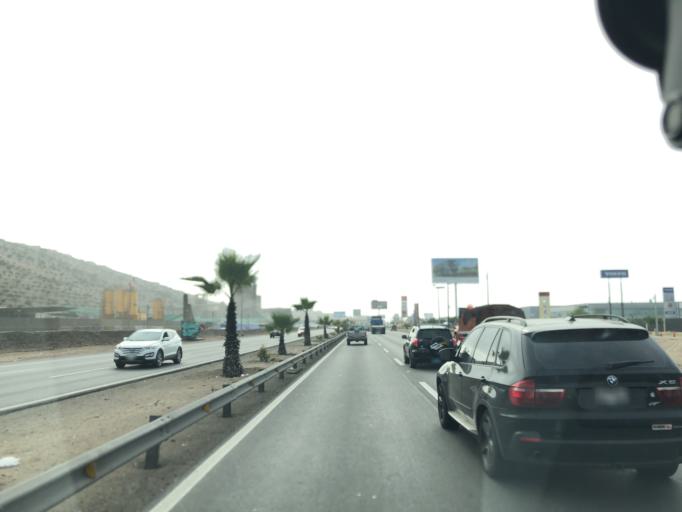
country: PE
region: Lima
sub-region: Lima
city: Surco
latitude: -12.2444
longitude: -76.9401
